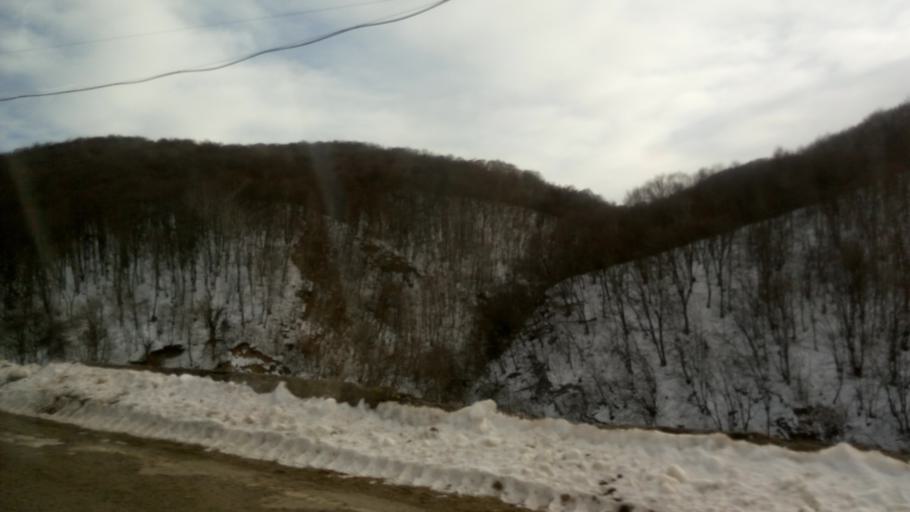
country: RU
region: Karachayevo-Cherkesiya
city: Karachayevsk
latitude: 43.7579
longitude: 42.0993
